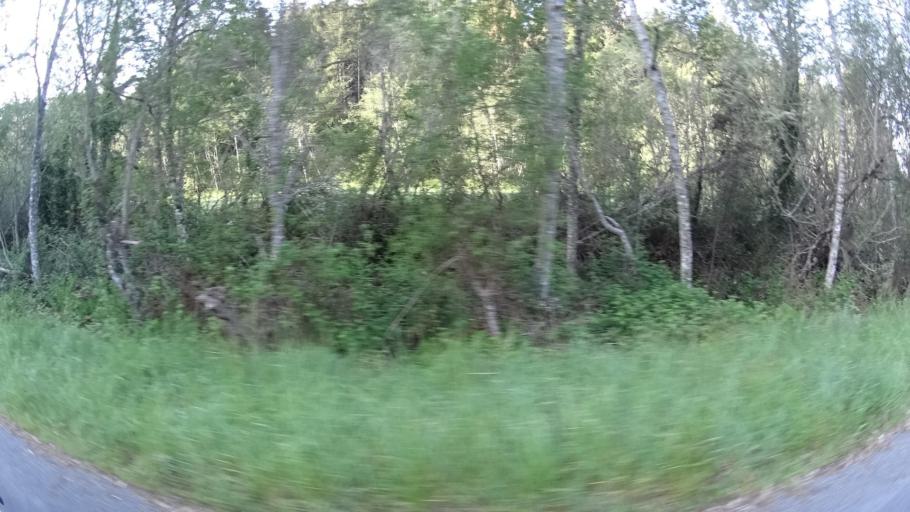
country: US
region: California
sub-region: Humboldt County
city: Myrtletown
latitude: 40.7772
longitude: -124.1161
